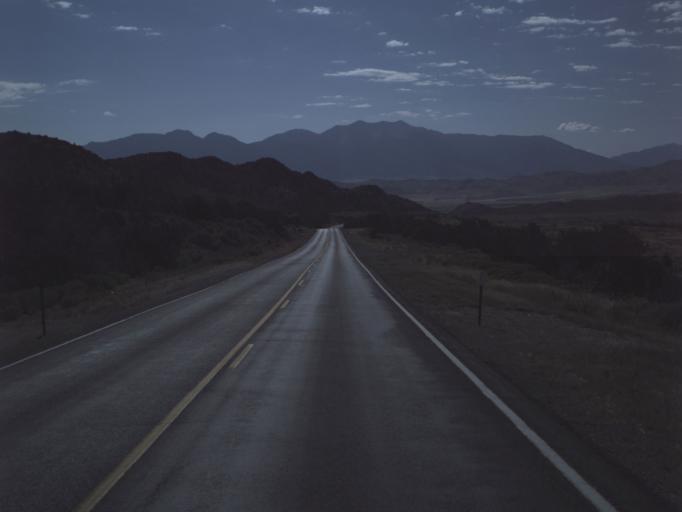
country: US
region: Utah
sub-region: Utah County
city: Genola
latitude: 39.9672
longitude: -112.0521
